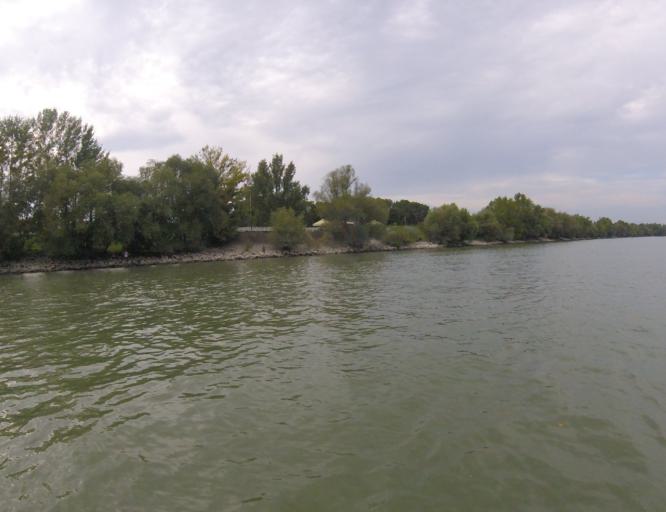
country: HU
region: Pest
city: Budakalasz
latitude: 47.5940
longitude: 19.0711
